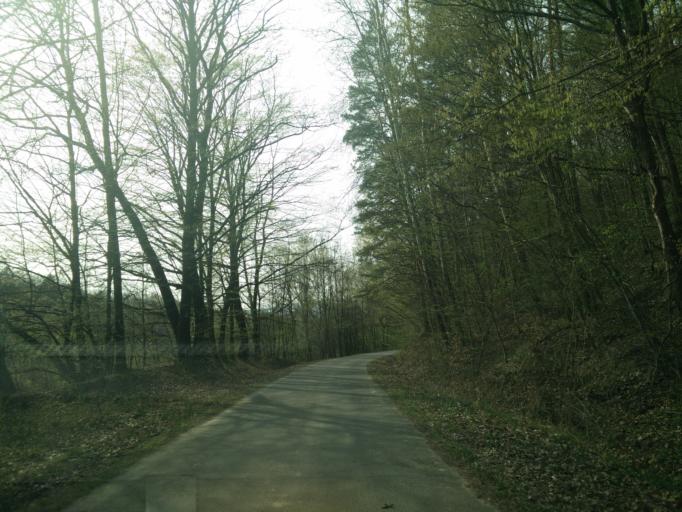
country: SK
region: Nitriansky
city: Prievidza
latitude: 48.8218
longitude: 18.6711
